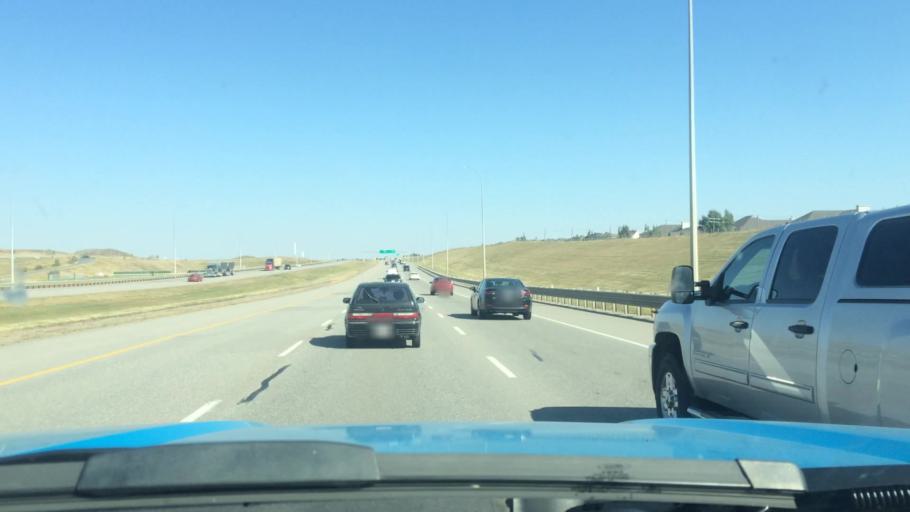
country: CA
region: Alberta
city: Calgary
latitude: 51.1506
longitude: -114.1866
